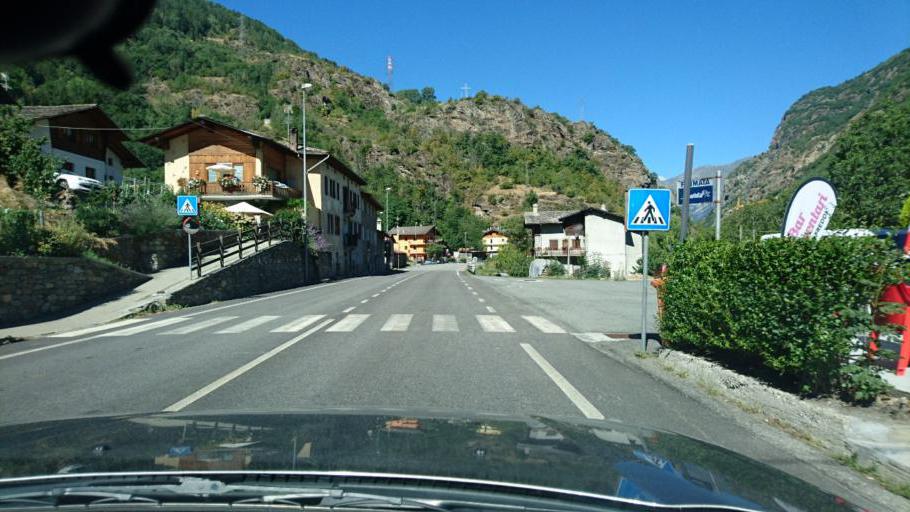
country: IT
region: Aosta Valley
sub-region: Valle d'Aosta
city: Avise
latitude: 45.7064
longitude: 7.1269
